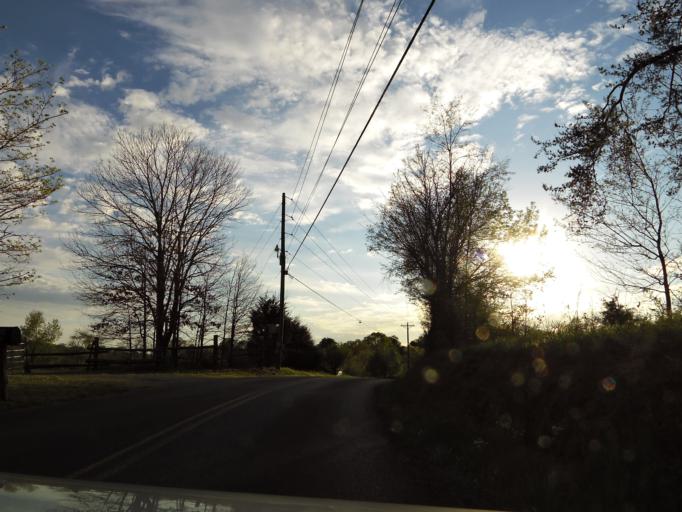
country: US
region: Tennessee
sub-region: Loudon County
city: Greenback
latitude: 35.6352
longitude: -84.0527
